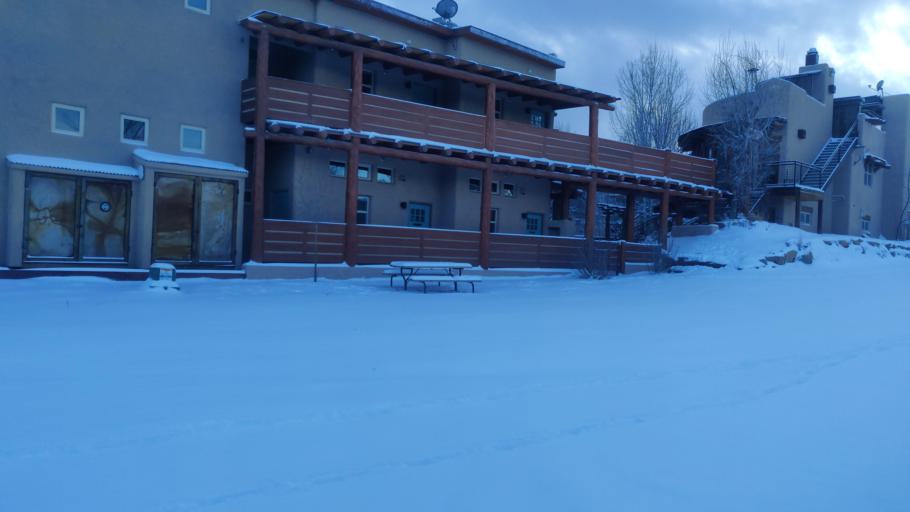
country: US
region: Colorado
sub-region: Ouray County
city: Ouray
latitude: 38.1492
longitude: -107.7551
